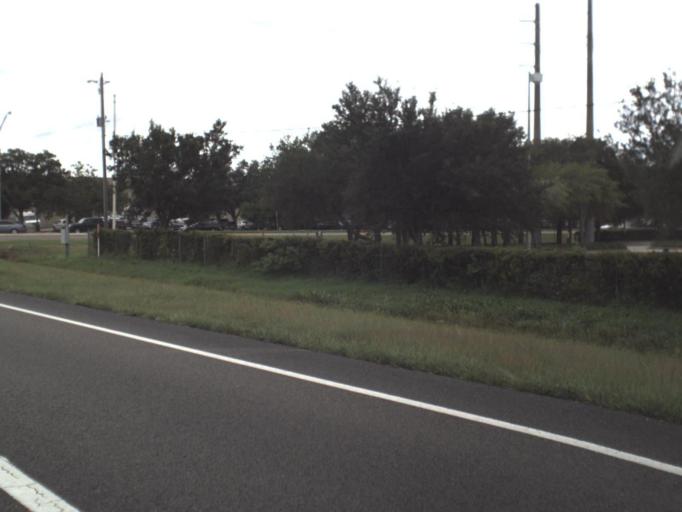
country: US
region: Florida
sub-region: Manatee County
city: Whitfield
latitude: 27.4300
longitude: -82.5306
